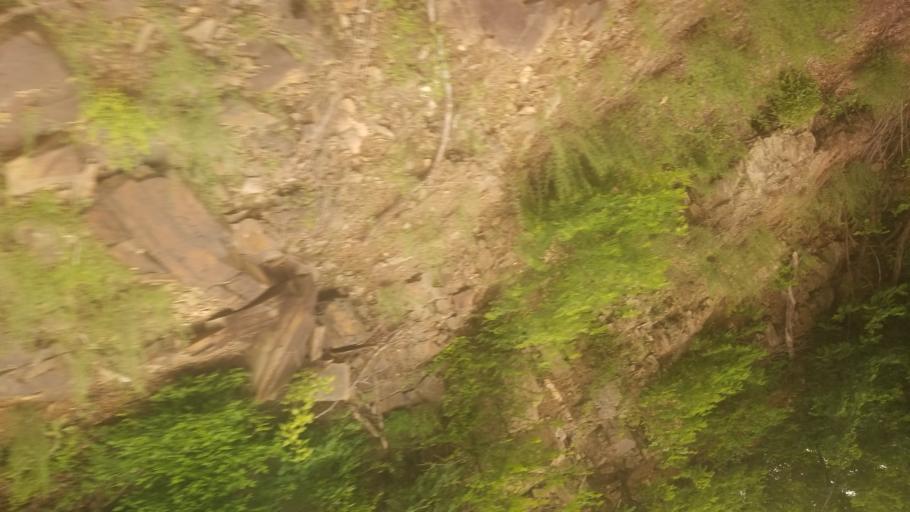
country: US
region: West Virginia
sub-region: Morgan County
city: Berkeley Springs
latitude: 39.6140
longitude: -78.3716
